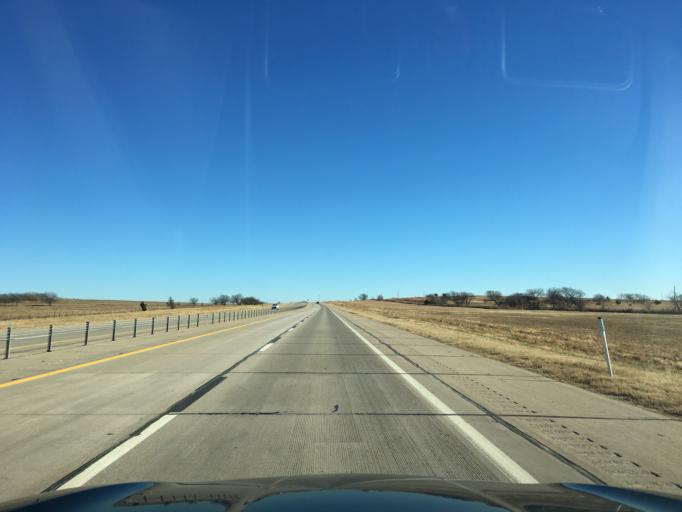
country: US
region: Oklahoma
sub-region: Noble County
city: Perry
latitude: 36.3924
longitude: -97.1888
